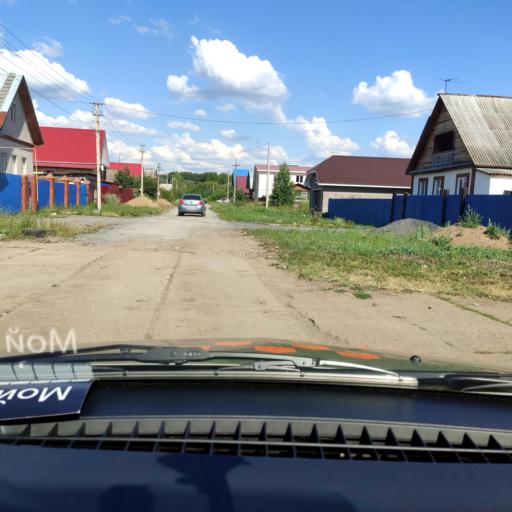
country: RU
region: Bashkortostan
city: Iglino
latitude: 54.8133
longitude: 56.1860
